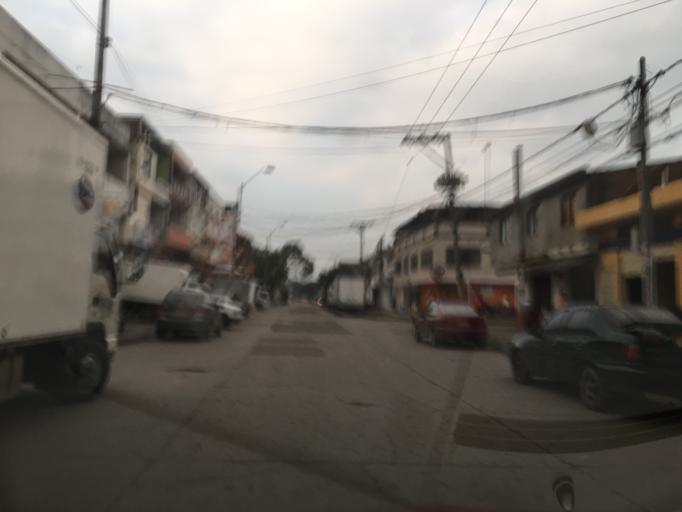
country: CO
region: Valle del Cauca
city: Cali
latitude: 3.4253
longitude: -76.5214
